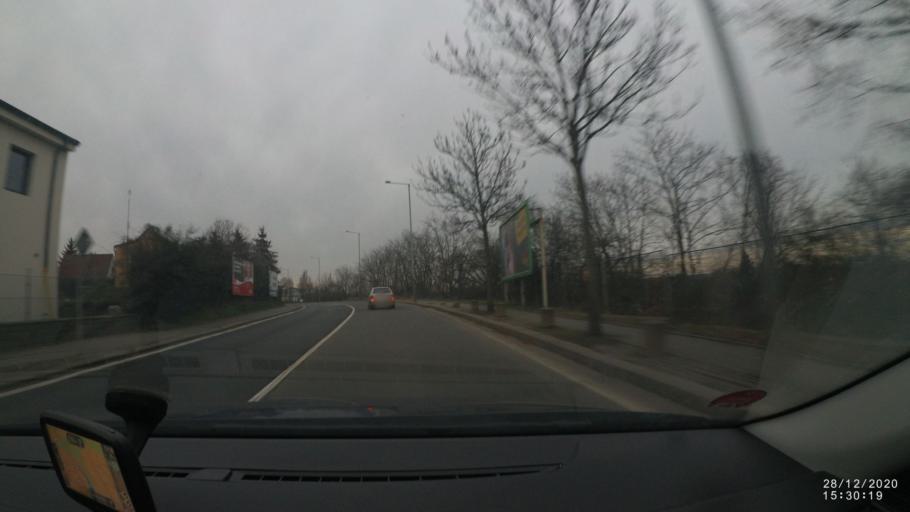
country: CZ
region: Praha
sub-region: Praha 14
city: Dolni Pocernice
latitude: 50.0868
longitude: 14.5732
